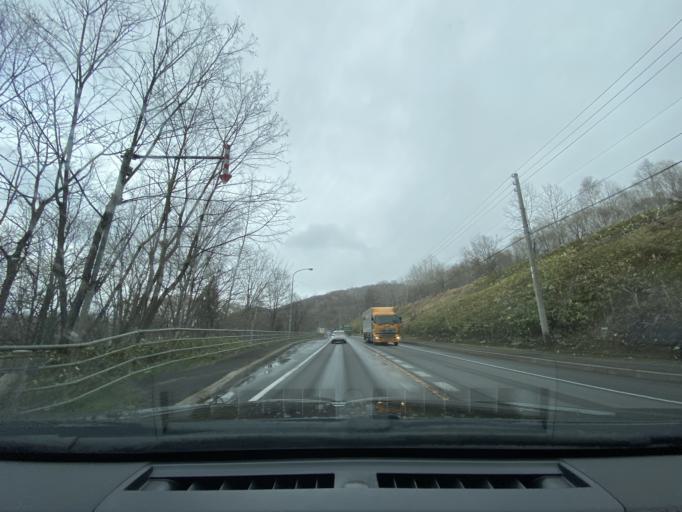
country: JP
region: Hokkaido
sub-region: Asahikawa-shi
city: Asahikawa
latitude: 43.7536
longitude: 142.2711
